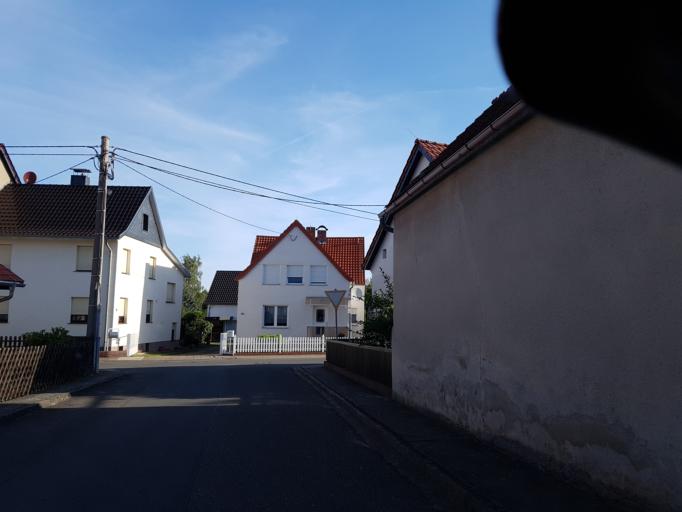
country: DE
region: Brandenburg
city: Elsterwerda
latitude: 51.4940
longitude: 13.5092
